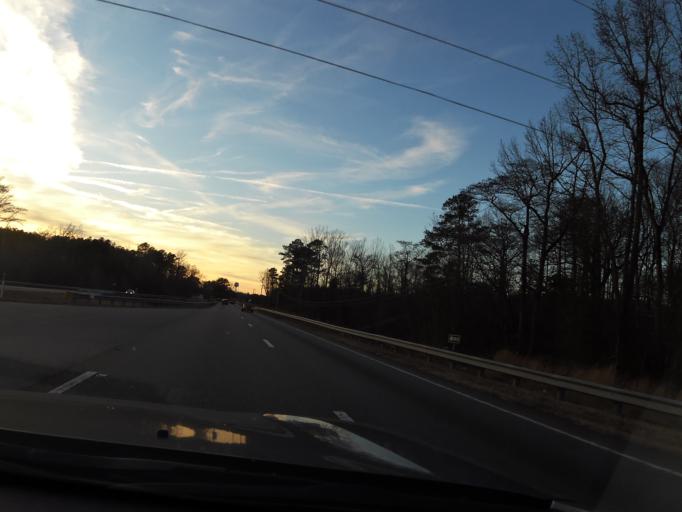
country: US
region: Virginia
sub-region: Southampton County
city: Courtland
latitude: 36.6830
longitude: -77.0131
